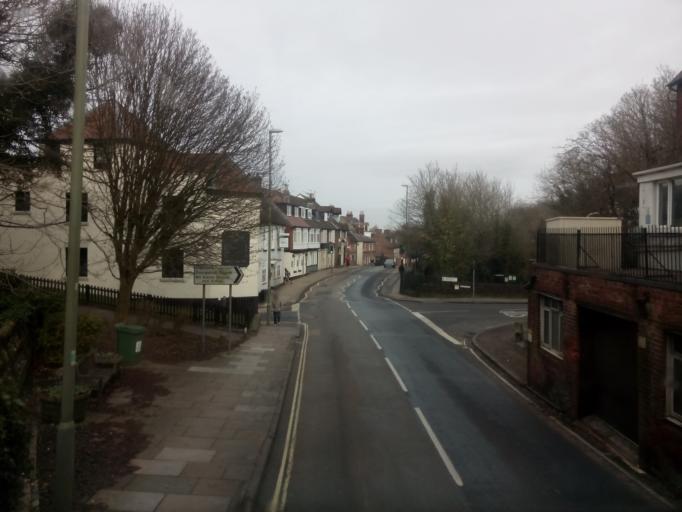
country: GB
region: England
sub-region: Hampshire
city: Winchester
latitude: 51.0574
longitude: -1.3066
